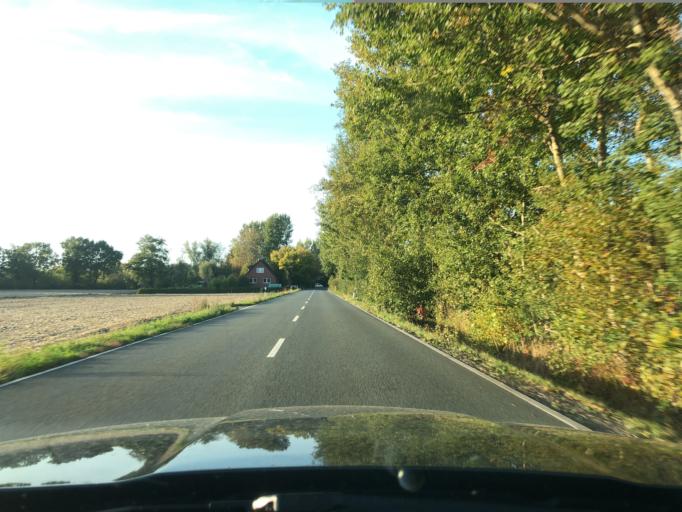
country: DE
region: North Rhine-Westphalia
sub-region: Regierungsbezirk Munster
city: Telgte
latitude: 51.9872
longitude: 7.7157
